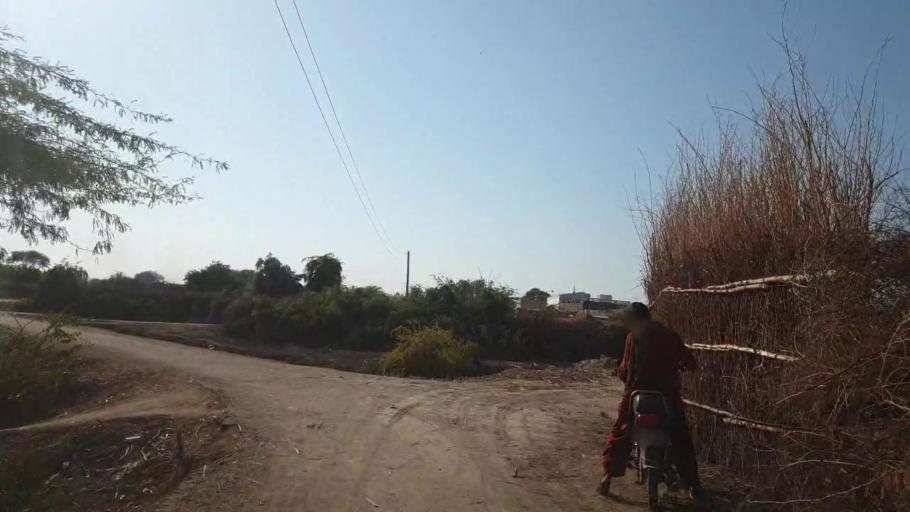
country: PK
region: Sindh
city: Mirpur Khas
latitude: 25.6275
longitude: 69.0689
